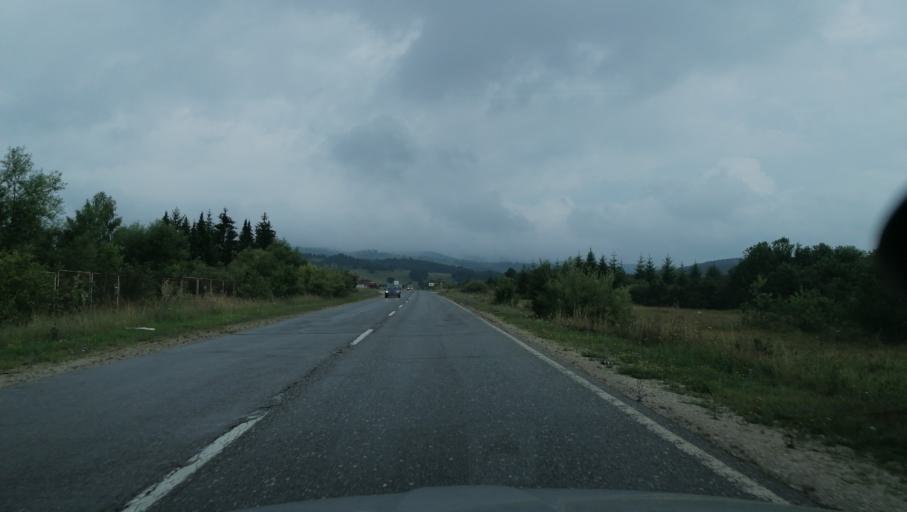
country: RS
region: Central Serbia
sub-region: Zlatiborski Okrug
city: Cajetina
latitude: 43.7872
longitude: 19.6911
